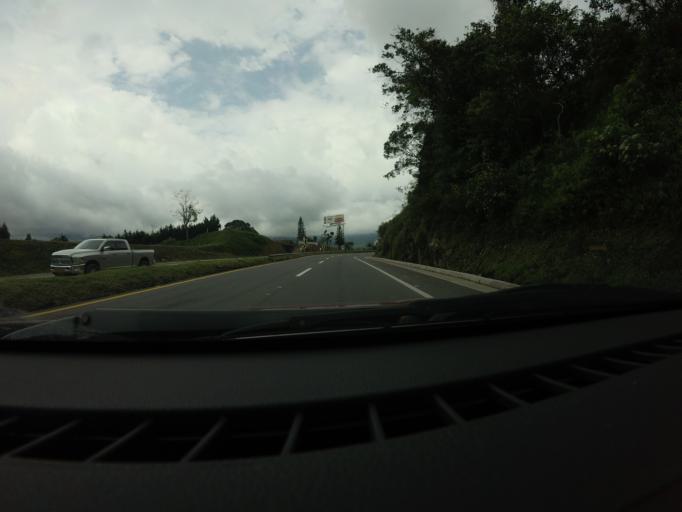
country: CO
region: Cundinamarca
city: San Francisco
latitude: 4.9637
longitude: -74.3040
